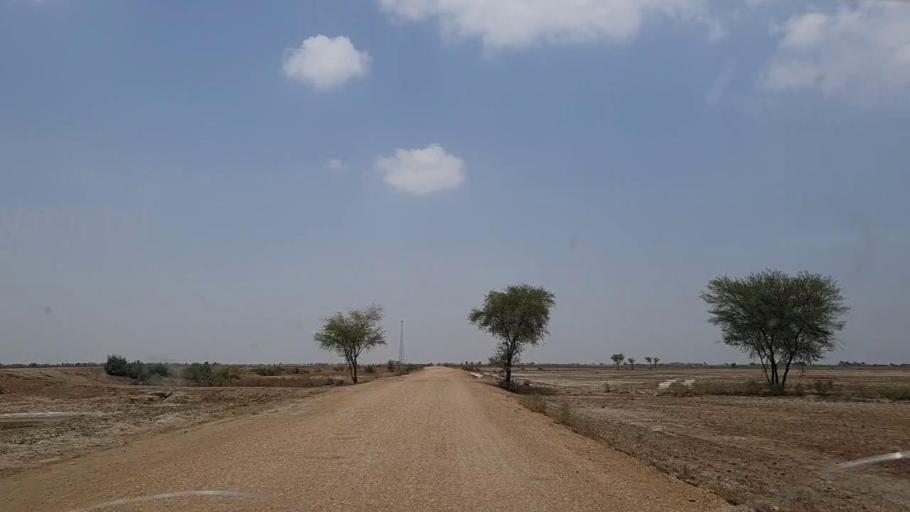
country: PK
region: Sindh
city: Johi
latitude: 26.7790
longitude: 67.6512
